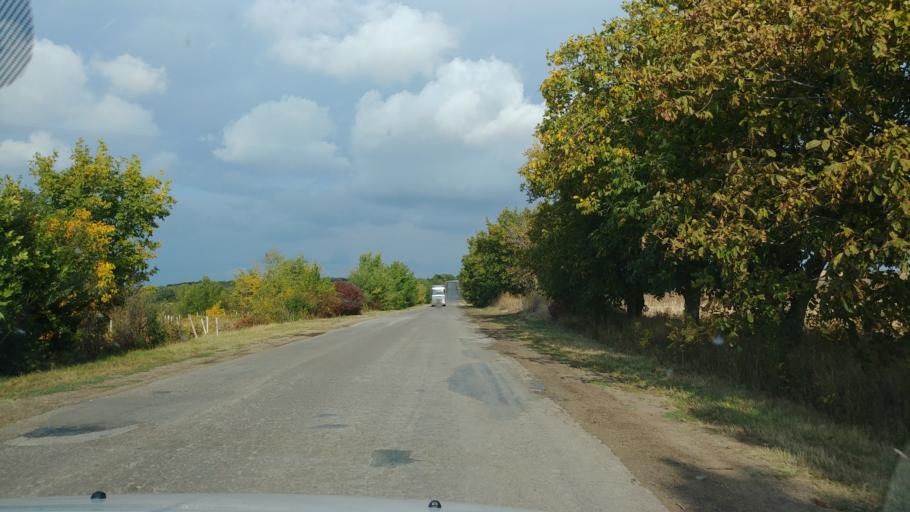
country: MD
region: Criuleni
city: Criuleni
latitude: 47.2156
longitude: 29.0730
